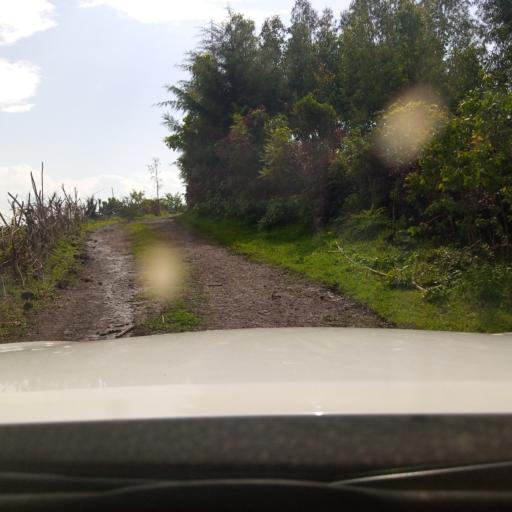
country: ET
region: Oromiya
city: Agaro
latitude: 7.9201
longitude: 36.7996
